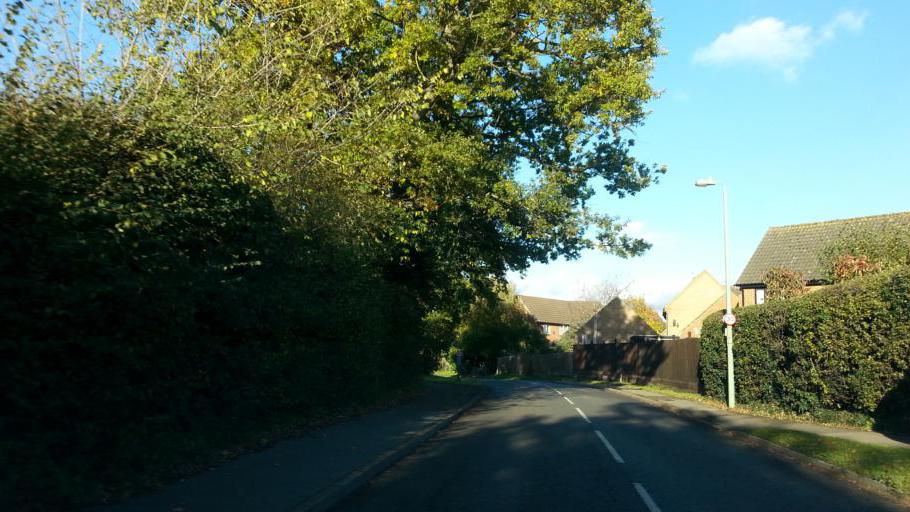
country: GB
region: England
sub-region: Suffolk
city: Thurston
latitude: 52.2530
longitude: 0.8111
